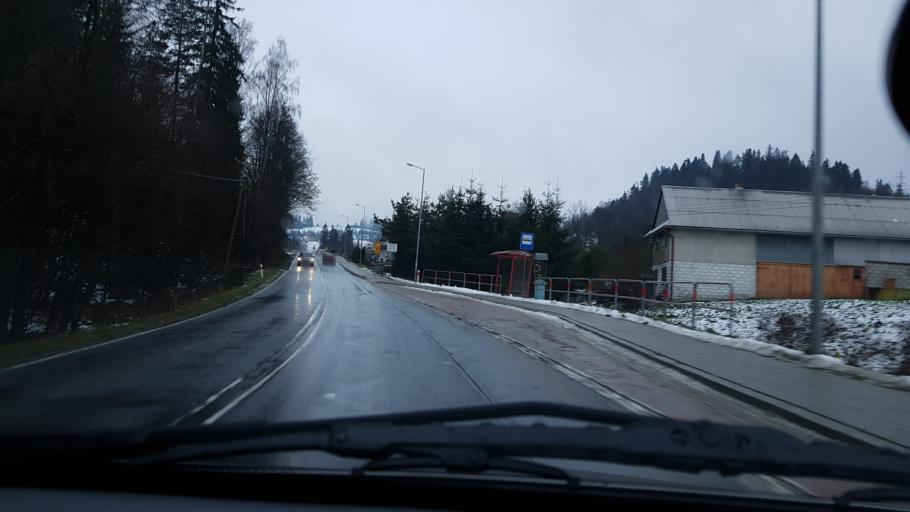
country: PL
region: Lesser Poland Voivodeship
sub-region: Powiat nowotarski
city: Raba Wyzna
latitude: 49.5321
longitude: 19.8871
